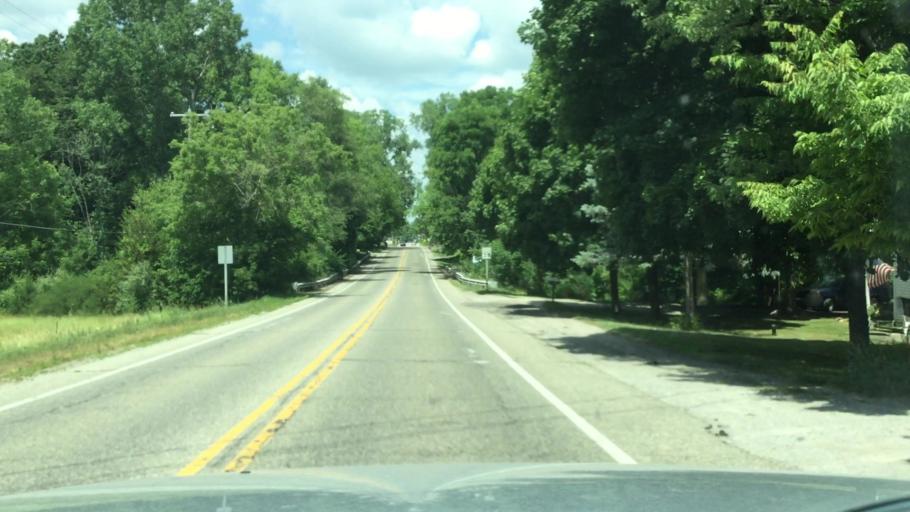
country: US
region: Michigan
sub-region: Genesee County
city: Flushing
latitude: 43.0651
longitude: -83.8646
